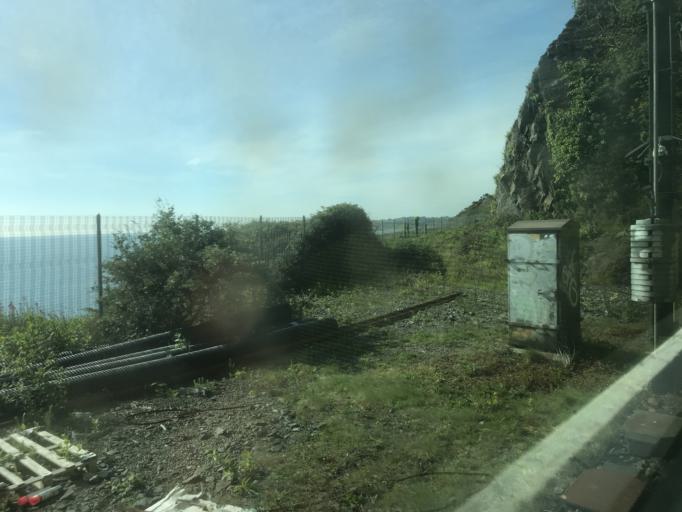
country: IE
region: Leinster
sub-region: Wicklow
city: Greystones
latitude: 53.1737
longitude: -6.0755
